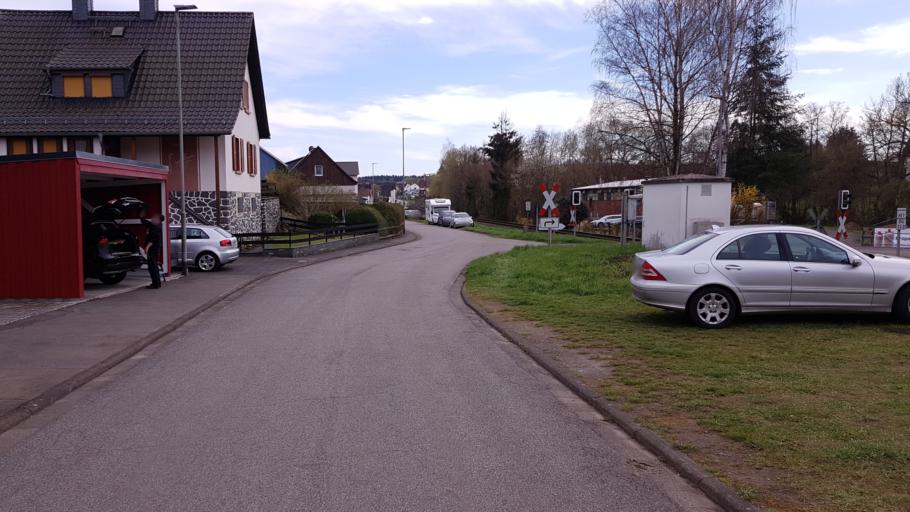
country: DE
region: Hesse
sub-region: Regierungsbezirk Giessen
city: Homberg
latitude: 50.6517
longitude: 9.0347
